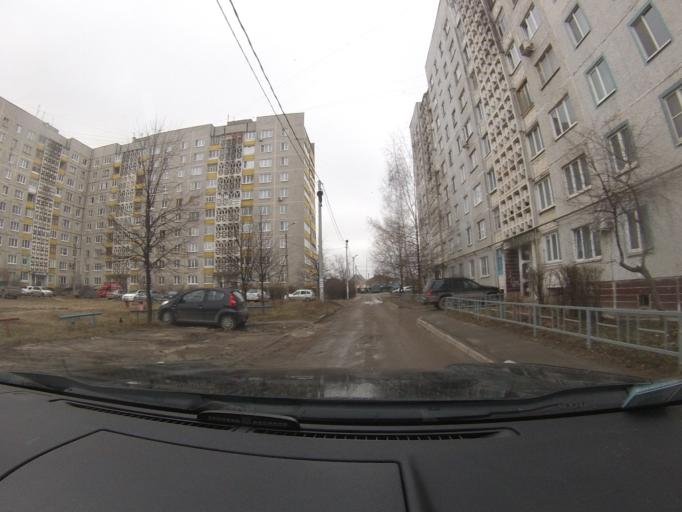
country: RU
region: Moskovskaya
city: Peski
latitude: 55.2708
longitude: 38.7518
